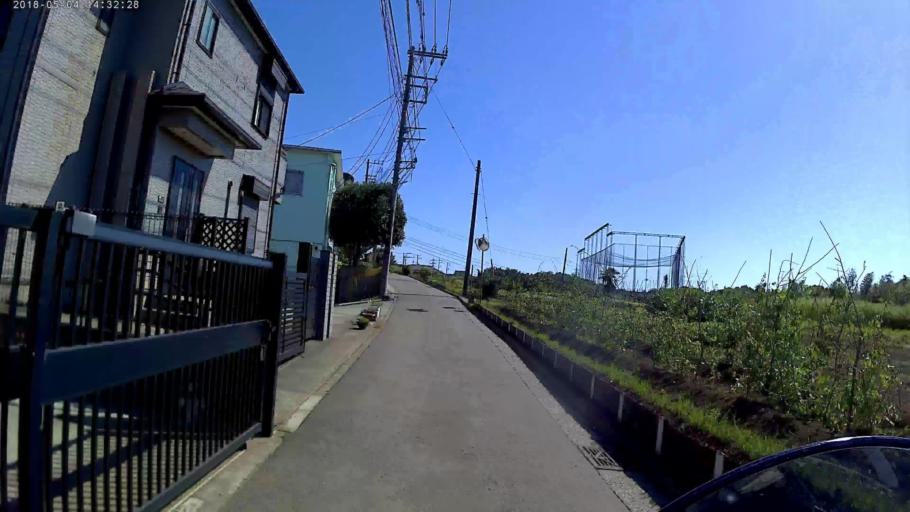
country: JP
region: Kanagawa
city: Yokohama
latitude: 35.4886
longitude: 139.6010
